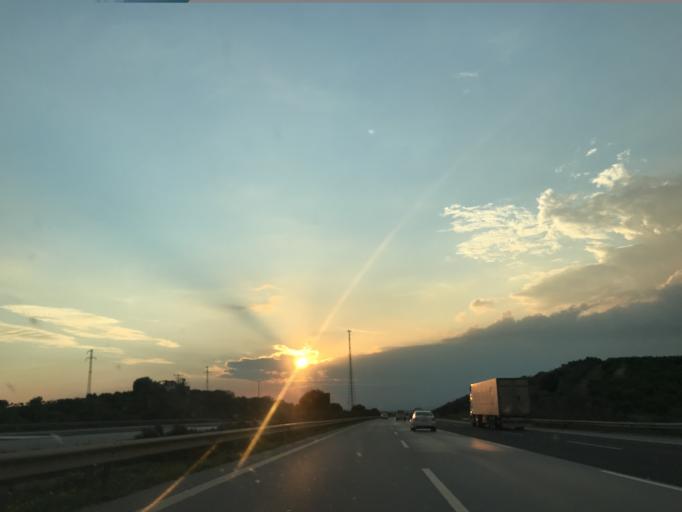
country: TR
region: Mersin
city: Yenice
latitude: 37.0234
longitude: 35.0952
